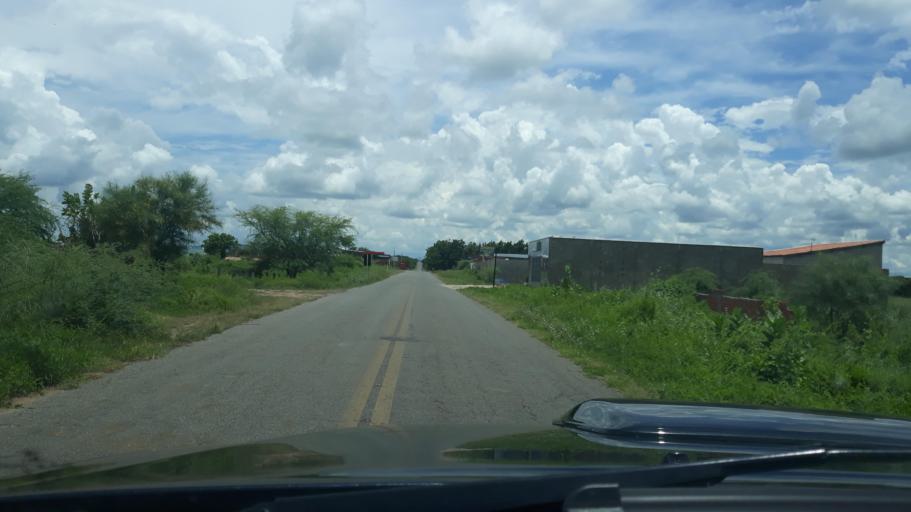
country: BR
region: Bahia
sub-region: Guanambi
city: Guanambi
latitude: -13.9141
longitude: -42.8439
